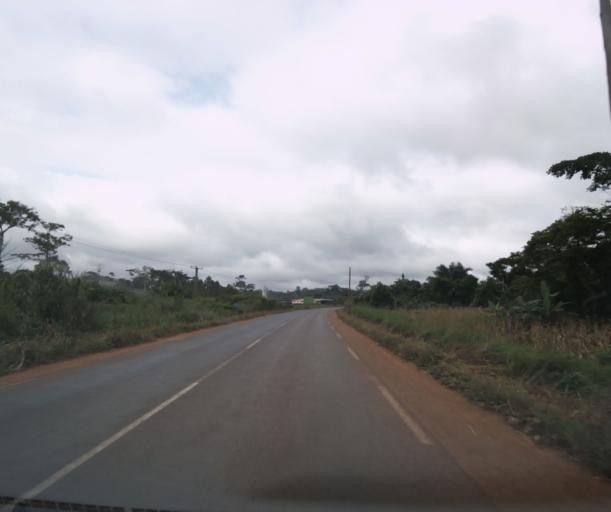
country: CM
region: Centre
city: Mbankomo
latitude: 3.7865
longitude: 11.4693
